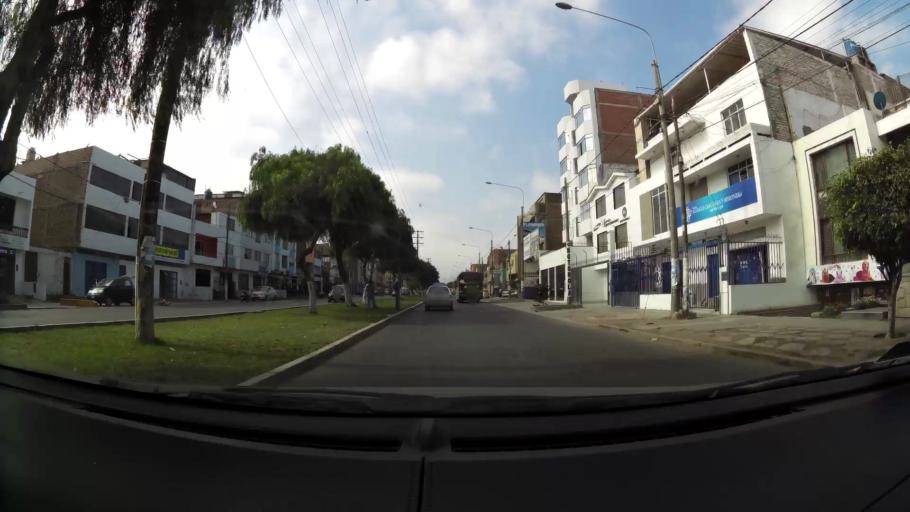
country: PE
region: La Libertad
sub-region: Provincia de Trujillo
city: Trujillo
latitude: -8.1086
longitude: -79.0120
